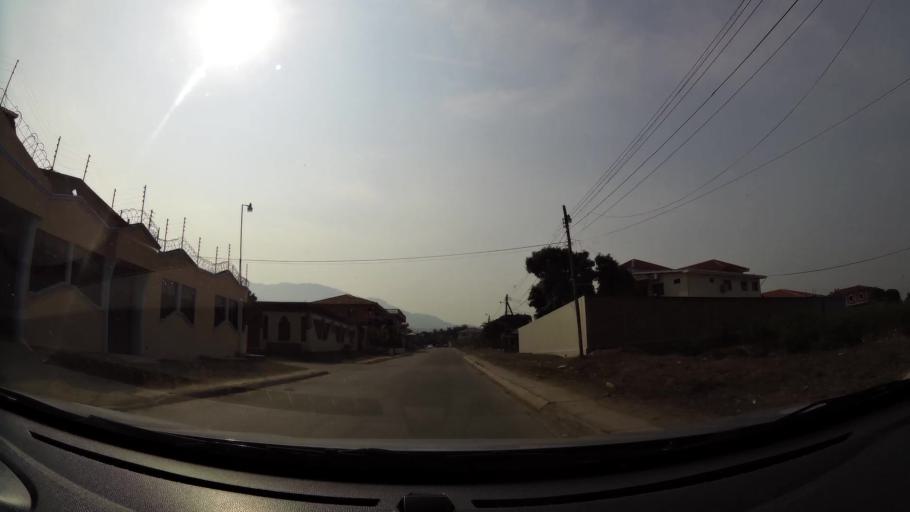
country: HN
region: Comayagua
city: Comayagua
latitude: 14.4515
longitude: -87.6204
